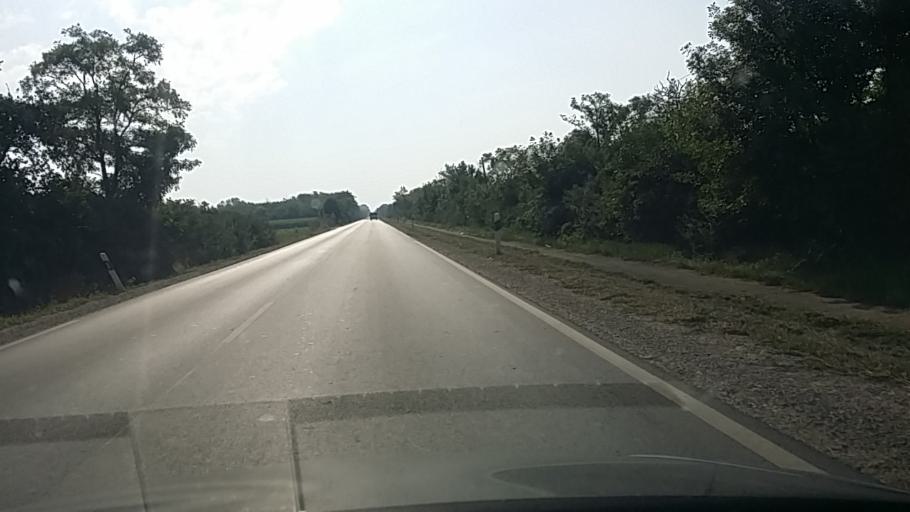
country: HU
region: Bekes
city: Kondoros
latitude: 46.7671
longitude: 20.7674
